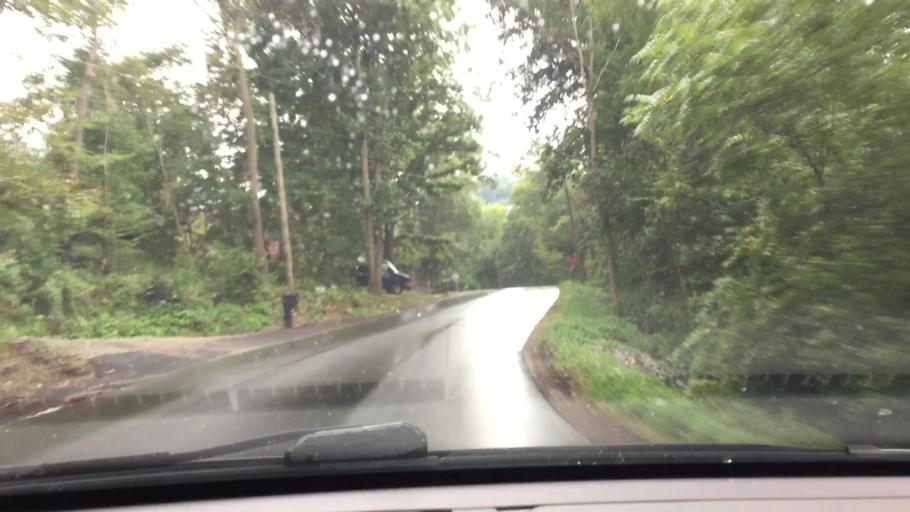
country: US
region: Pennsylvania
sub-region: Washington County
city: Canonsburg
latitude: 40.2776
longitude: -80.1923
